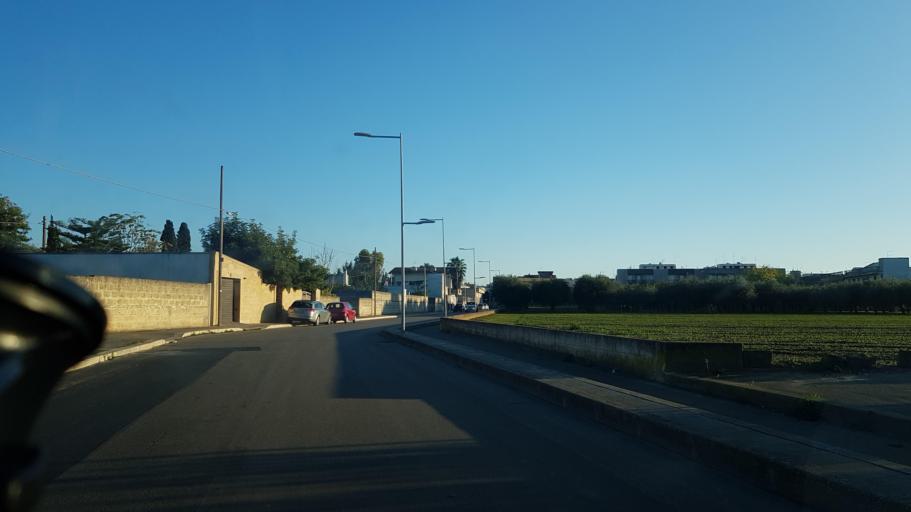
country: IT
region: Apulia
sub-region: Provincia di Brindisi
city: Latiano
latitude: 40.5566
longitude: 17.7236
